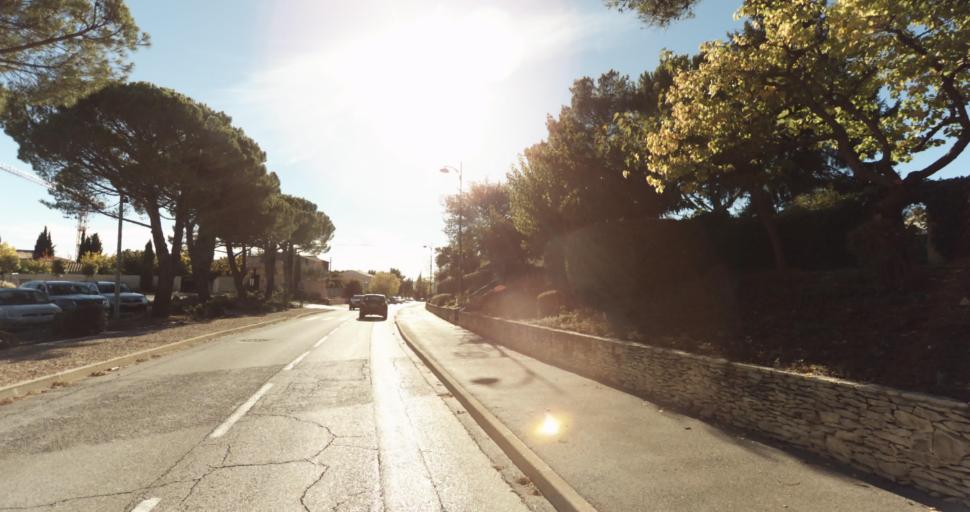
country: FR
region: Provence-Alpes-Cote d'Azur
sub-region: Departement des Bouches-du-Rhone
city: Venelles
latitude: 43.5964
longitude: 5.4841
